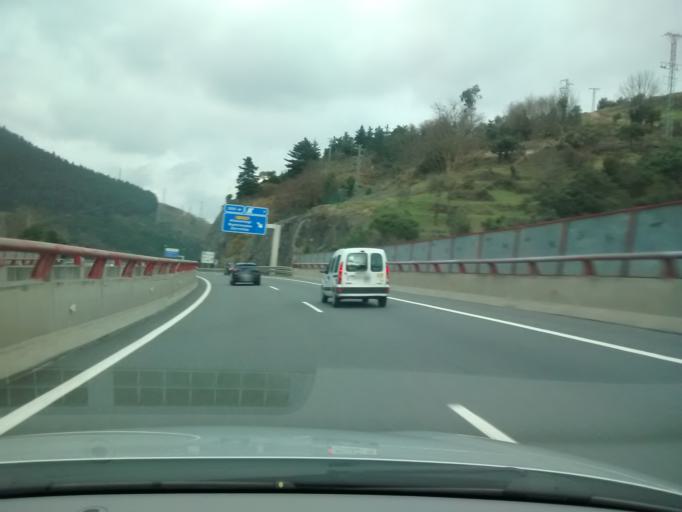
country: ES
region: Basque Country
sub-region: Bizkaia
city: Alonsotegi
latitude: 43.2423
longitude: -2.9878
